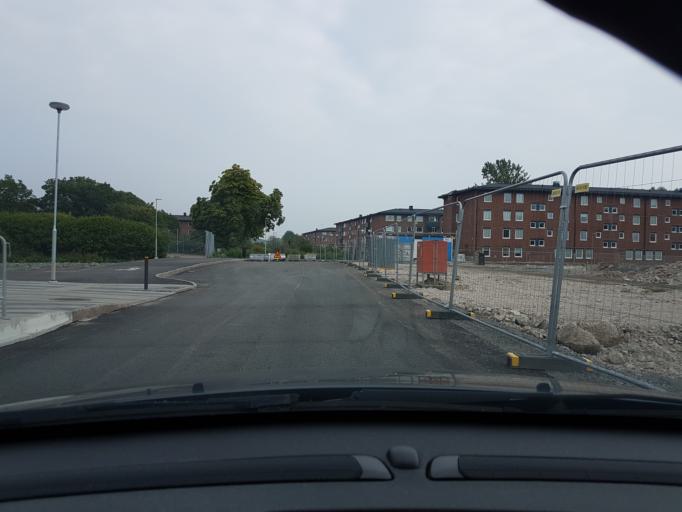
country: SE
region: Vaestra Goetaland
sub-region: Goteborg
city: Majorna
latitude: 57.6417
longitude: 11.9013
